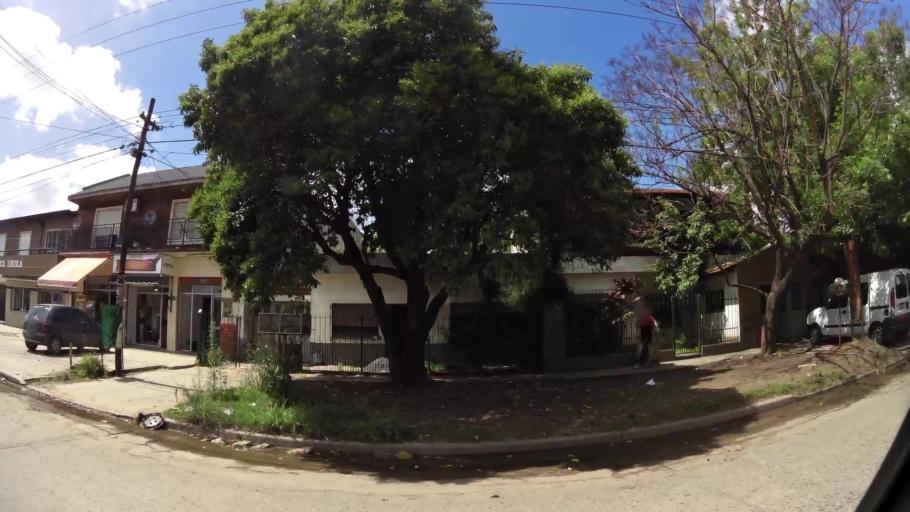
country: AR
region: Buenos Aires
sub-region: Partido de Quilmes
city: Quilmes
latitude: -34.8282
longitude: -58.2278
